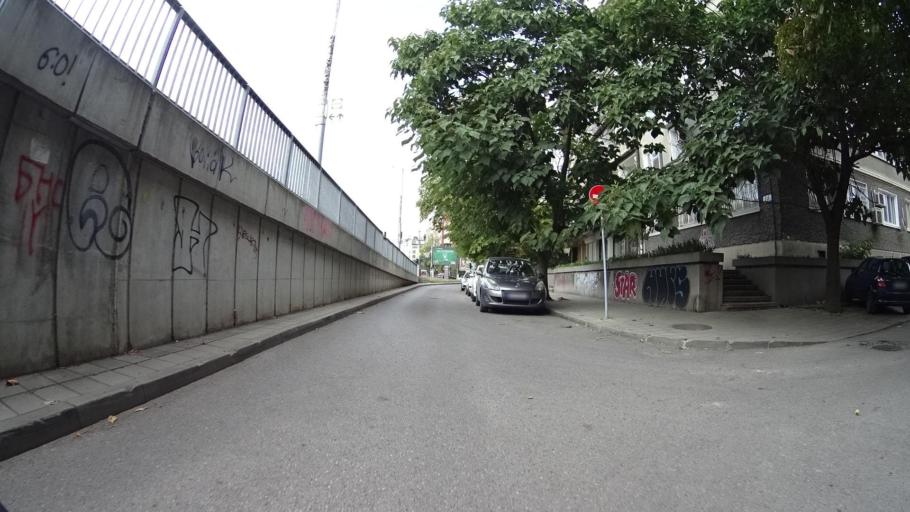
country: BG
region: Plovdiv
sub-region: Obshtina Plovdiv
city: Plovdiv
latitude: 42.1550
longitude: 24.7391
